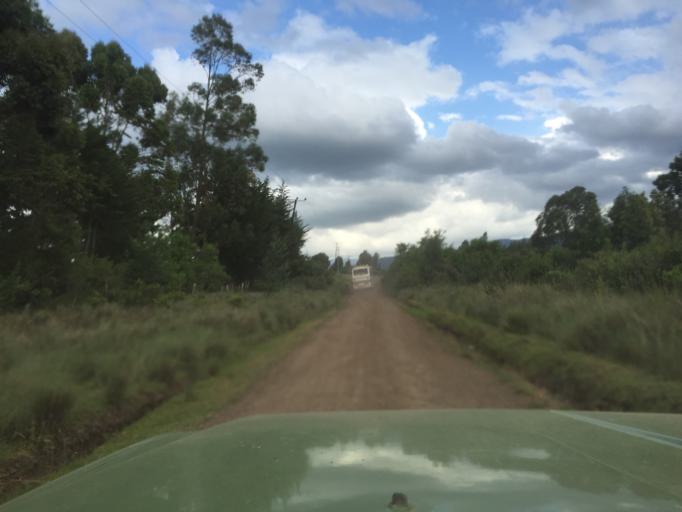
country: KE
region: Nyandarua
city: Ol Kalou
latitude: -0.4161
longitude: 36.4522
